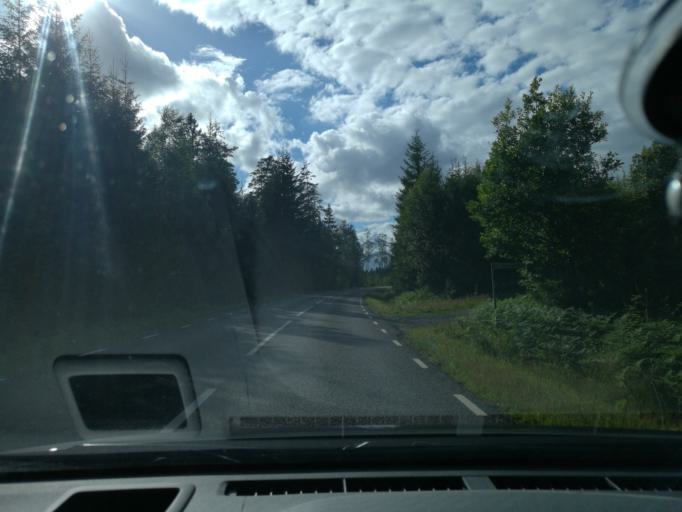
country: SE
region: Kronoberg
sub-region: Vaxjo Kommun
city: Braas
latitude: 57.0647
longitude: 15.0156
